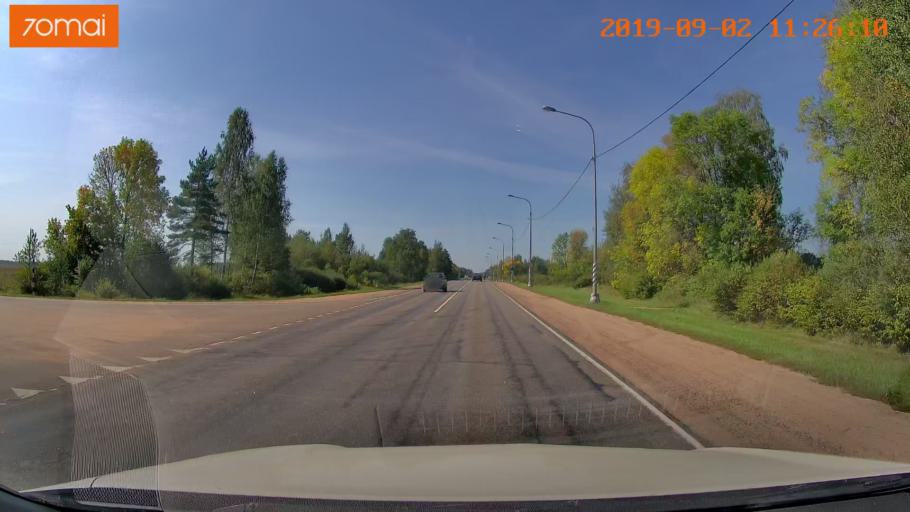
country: RU
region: Smolensk
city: Roslavl'
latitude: 53.9945
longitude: 32.9362
